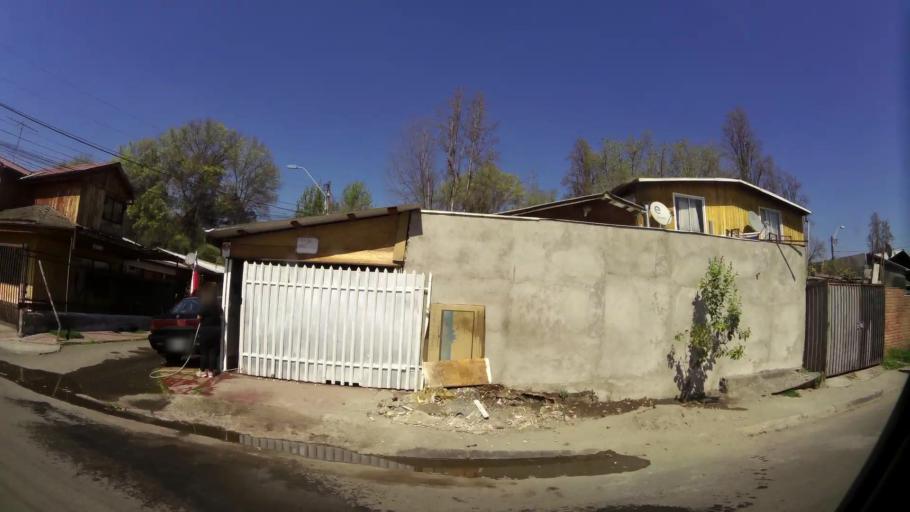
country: CL
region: Santiago Metropolitan
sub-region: Provincia de Talagante
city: Penaflor
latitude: -33.5740
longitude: -70.8178
